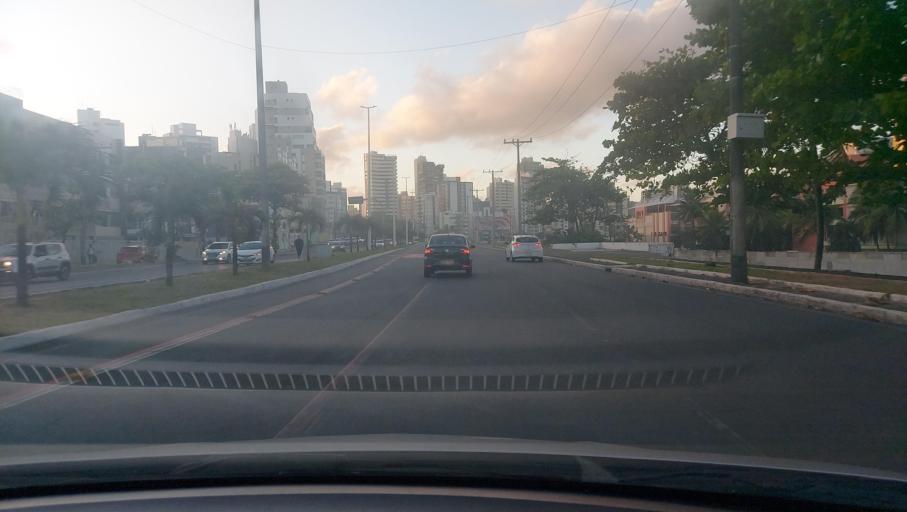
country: BR
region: Bahia
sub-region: Salvador
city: Salvador
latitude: -12.9981
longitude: -38.4491
